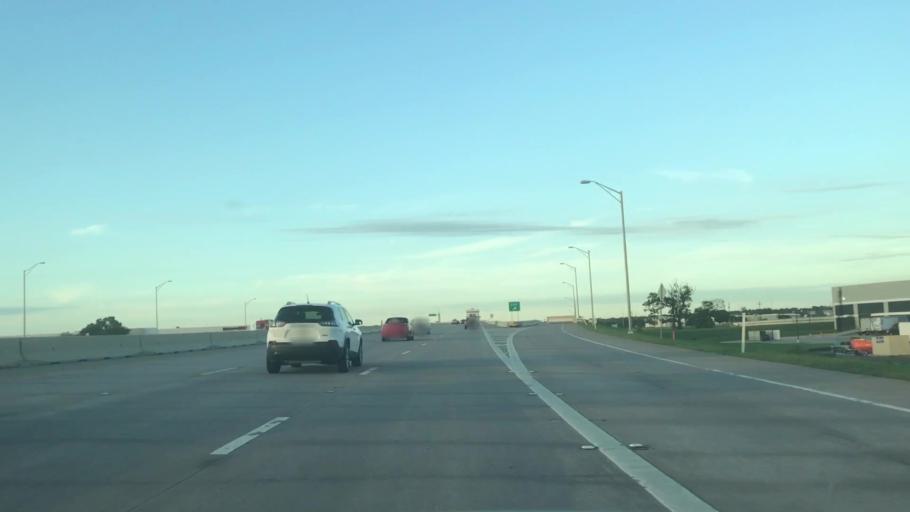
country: US
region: Texas
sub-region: Dallas County
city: Farmers Branch
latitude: 32.9446
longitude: -96.9287
